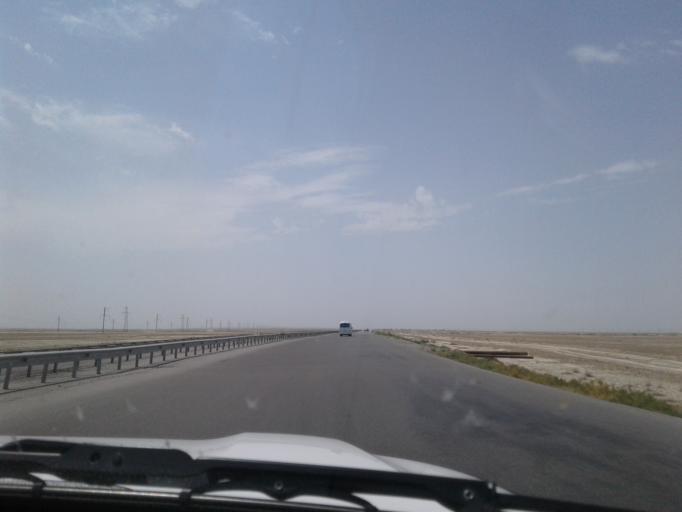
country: TM
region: Ahal
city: Kaka
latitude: 37.2700
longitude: 59.8233
